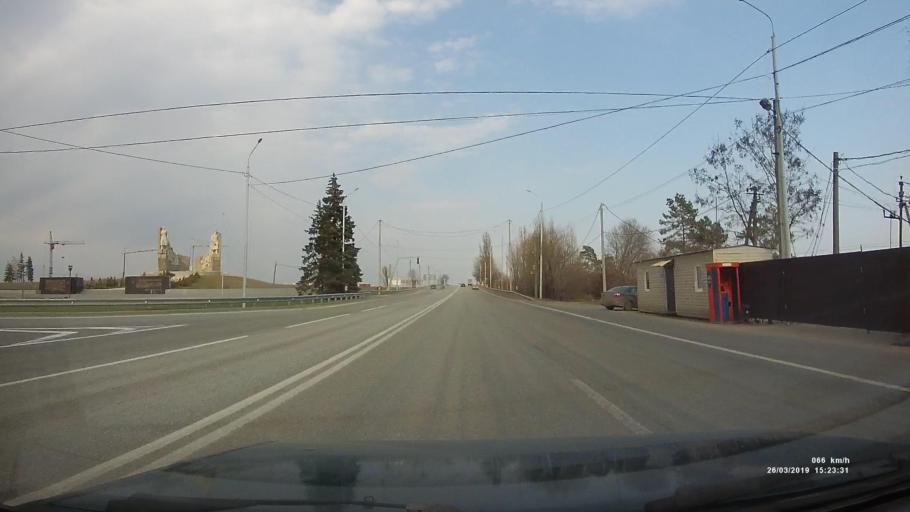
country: RU
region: Rostov
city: Primorka
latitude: 47.3148
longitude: 39.0098
